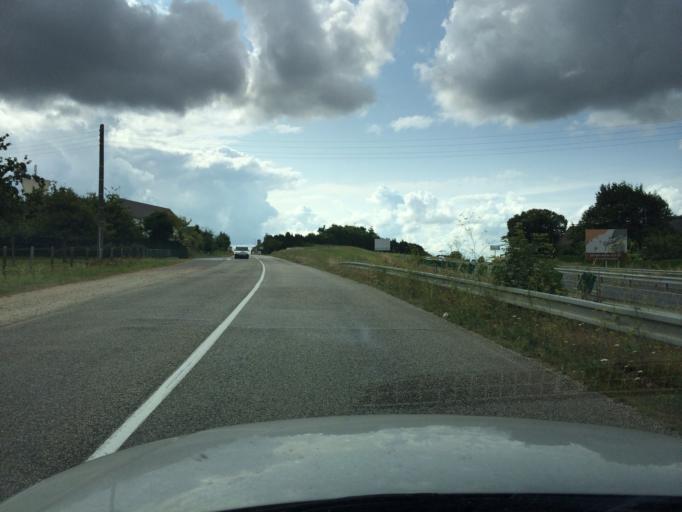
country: FR
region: Lower Normandy
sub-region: Departement de la Manche
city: Sainte-Mere-Eglise
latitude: 49.4143
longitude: -1.3221
